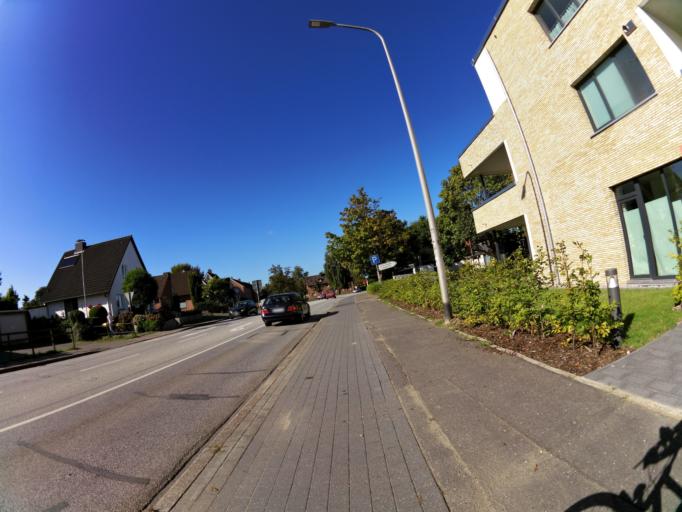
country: DE
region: Schleswig-Holstein
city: Eckernforde
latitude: 54.4555
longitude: 9.8347
